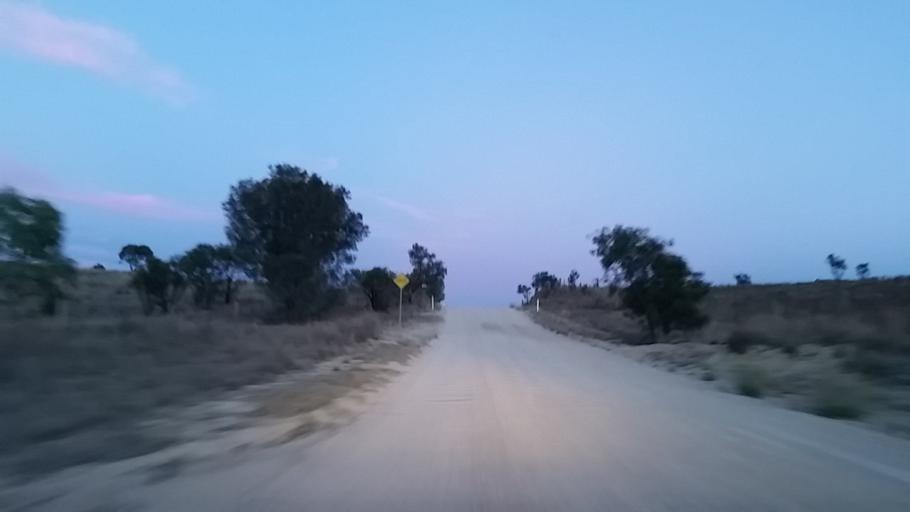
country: AU
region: South Australia
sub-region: Mount Barker
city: Callington
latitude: -35.1063
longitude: 139.0224
